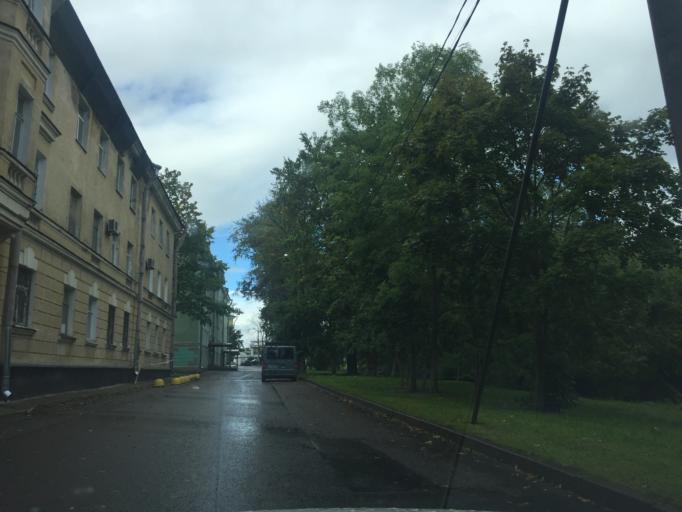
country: RU
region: St.-Petersburg
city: Krasnoye Selo
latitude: 59.7369
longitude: 30.0929
